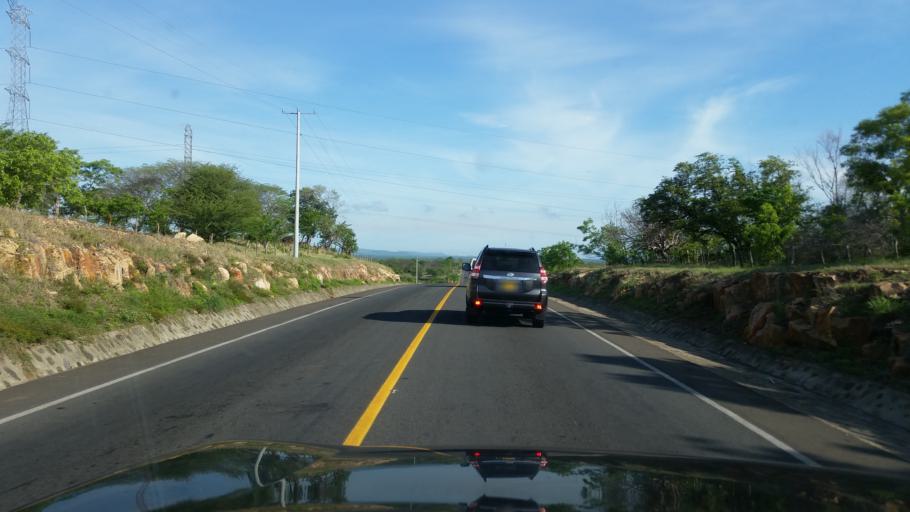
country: NI
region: Leon
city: La Paz Centro
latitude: 12.2329
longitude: -86.7054
